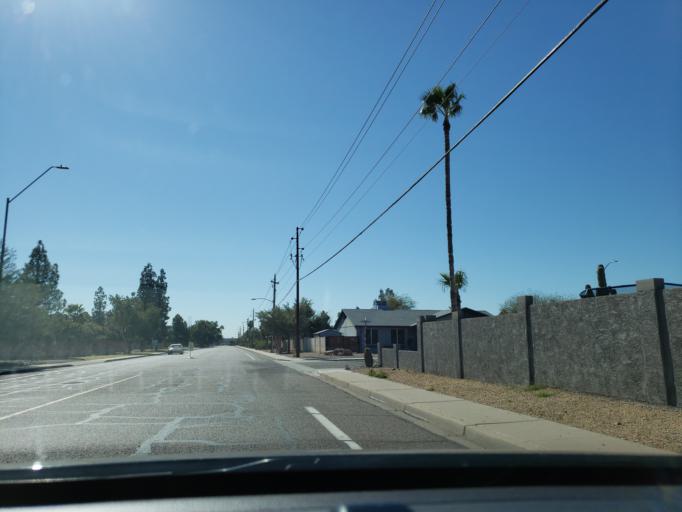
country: US
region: Arizona
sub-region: Maricopa County
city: Glendale
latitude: 33.6514
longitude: -112.1172
